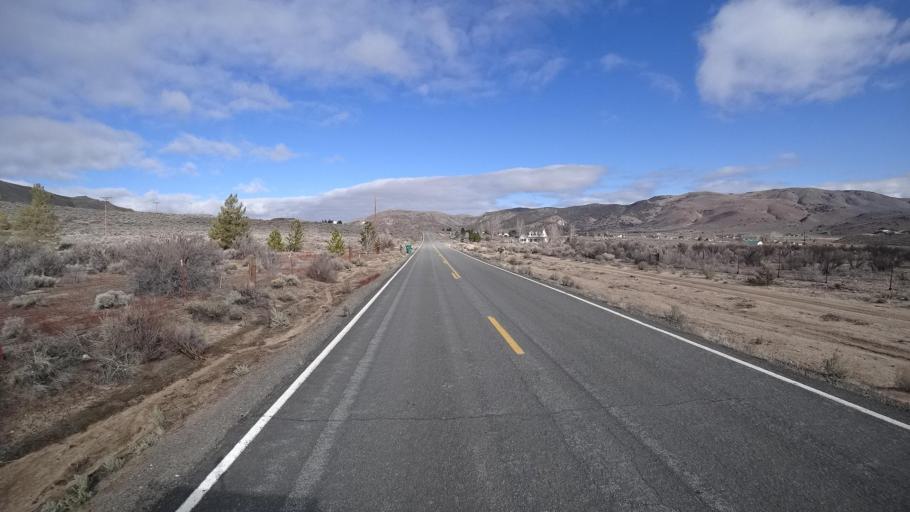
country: US
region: Nevada
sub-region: Washoe County
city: Cold Springs
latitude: 39.8811
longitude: -119.9677
